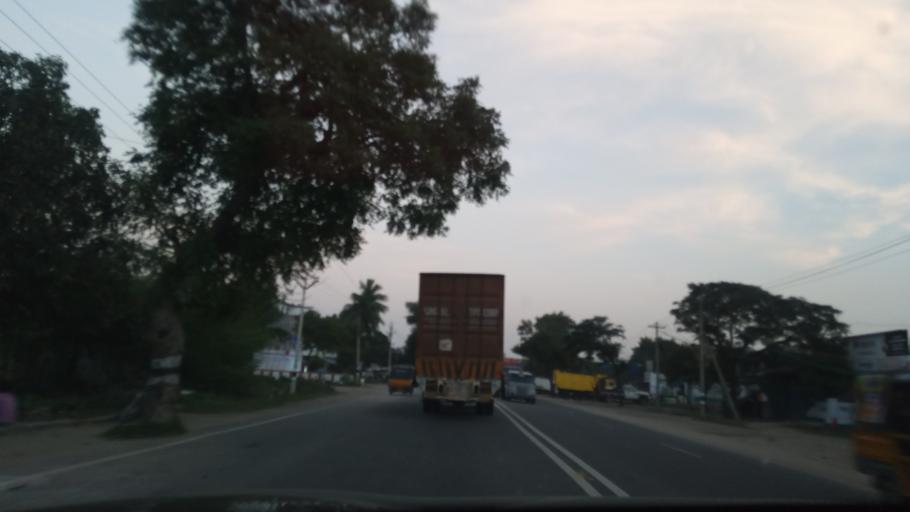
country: IN
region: Tamil Nadu
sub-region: Vellore
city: Walajapet
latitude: 12.9290
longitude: 79.3432
